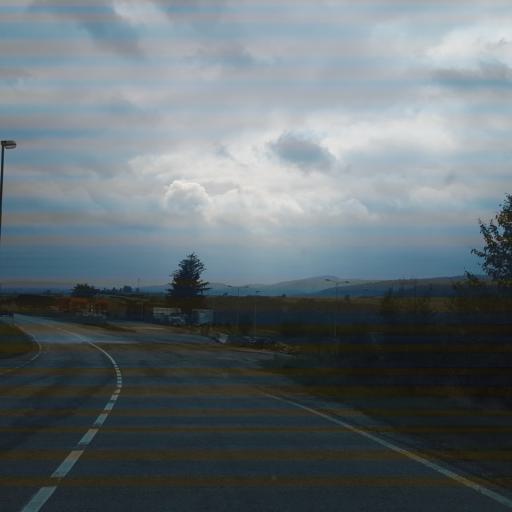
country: RS
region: Central Serbia
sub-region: Nisavski Okrug
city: Razanj
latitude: 43.6825
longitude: 21.5467
